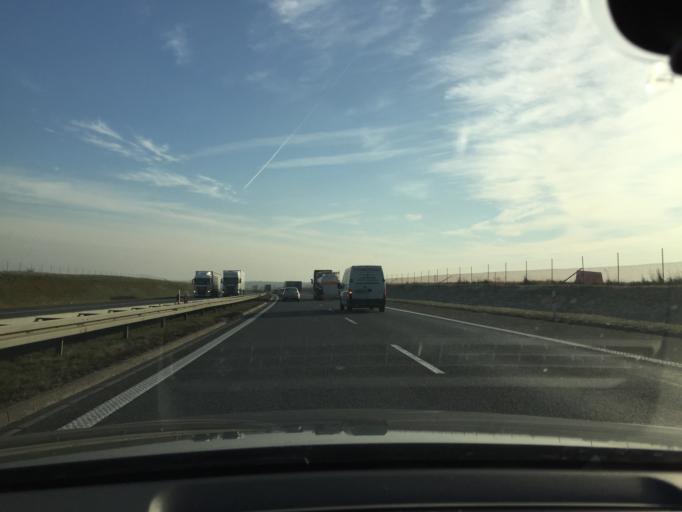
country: PL
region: Silesian Voivodeship
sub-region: Powiat gliwicki
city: Zernica
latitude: 50.2719
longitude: 18.5785
